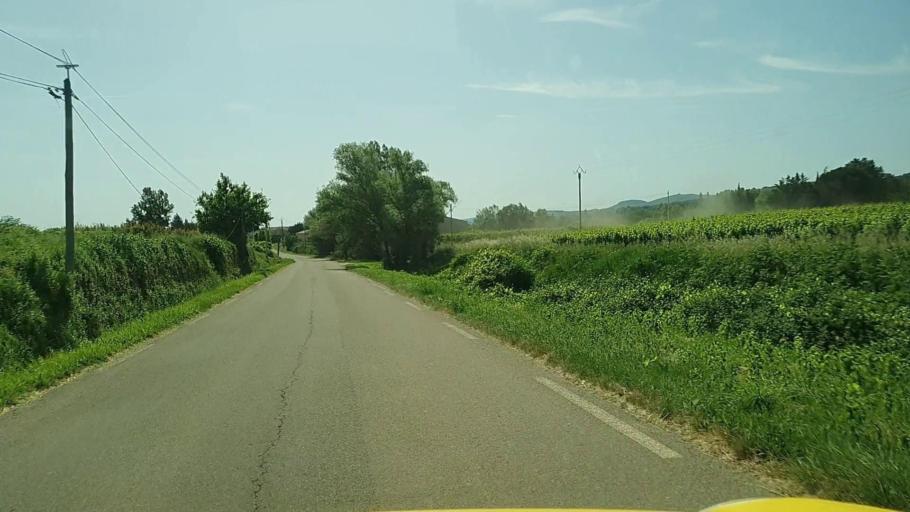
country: FR
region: Languedoc-Roussillon
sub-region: Departement du Gard
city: Sabran
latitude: 44.1170
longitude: 4.5106
